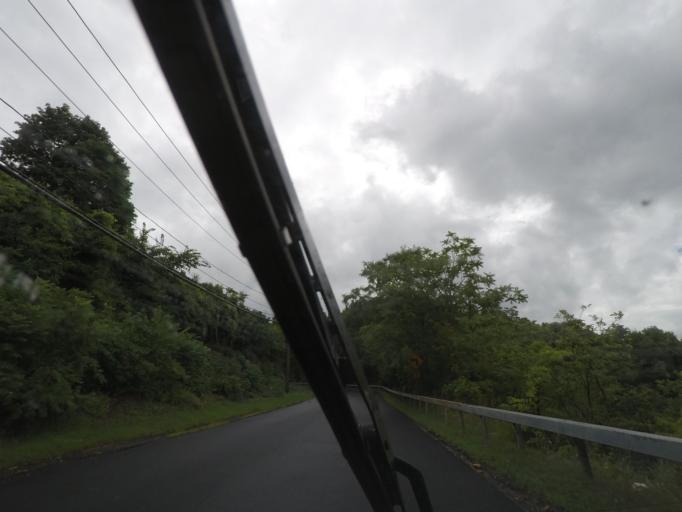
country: US
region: New York
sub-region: Rensselaer County
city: Rensselaer
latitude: 42.6352
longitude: -73.7370
